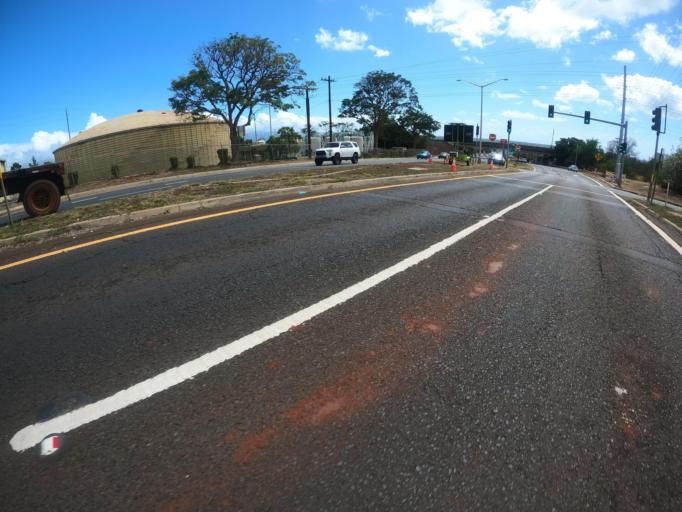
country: US
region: Hawaii
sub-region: Honolulu County
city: Royal Kunia
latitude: 21.3850
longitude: -158.0331
